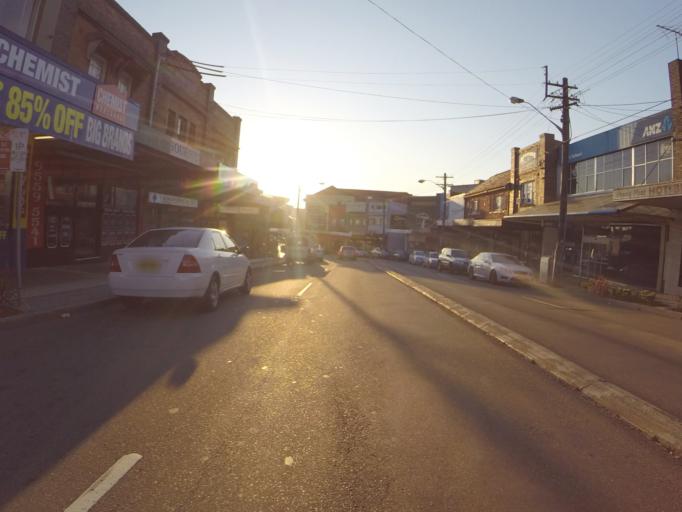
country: AU
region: New South Wales
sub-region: Rockdale
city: Bardwell Valley
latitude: -33.9265
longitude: 151.1265
